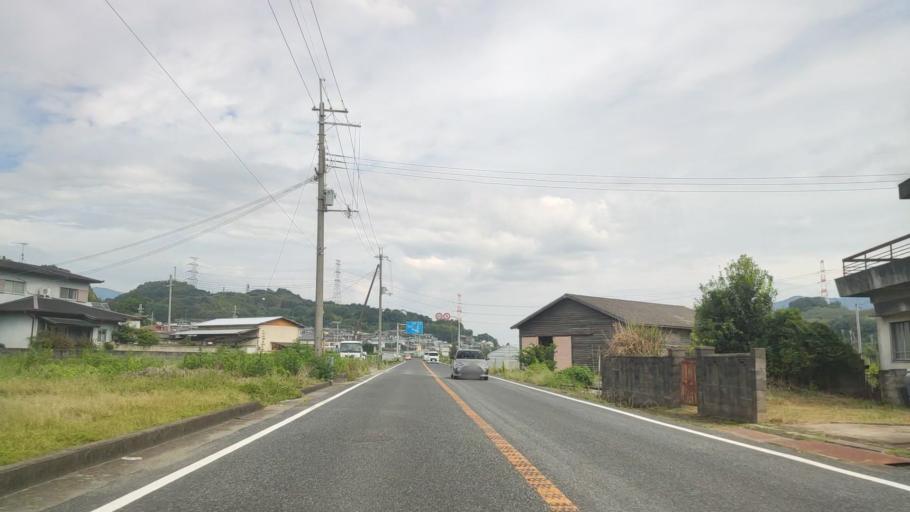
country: JP
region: Wakayama
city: Iwade
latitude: 34.2770
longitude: 135.4446
